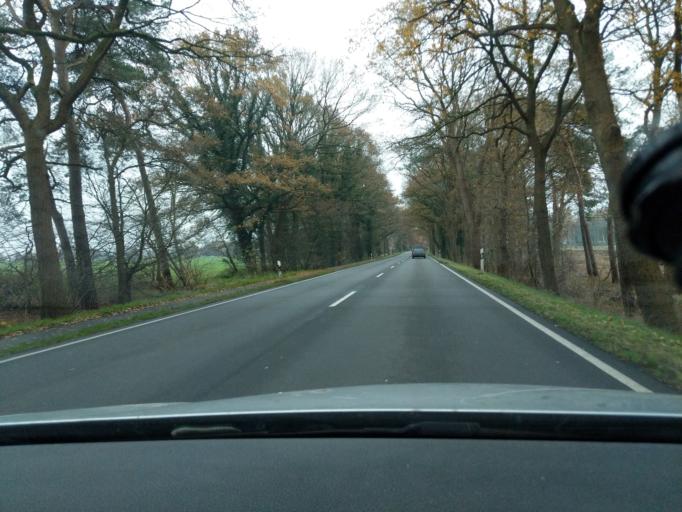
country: DE
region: Lower Saxony
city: Gyhum
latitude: 53.2199
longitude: 9.2946
